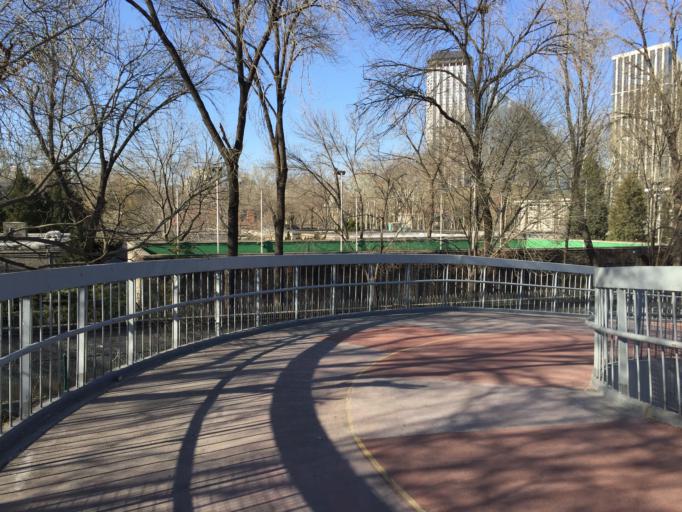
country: CN
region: Beijing
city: Chaowai
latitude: 39.9431
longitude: 116.4552
